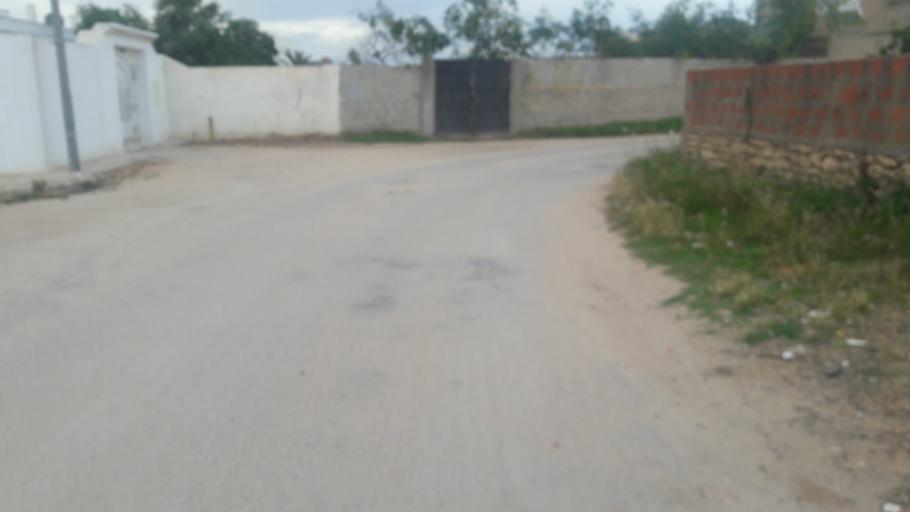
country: TN
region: Safaqis
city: Al Qarmadah
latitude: 34.8104
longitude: 10.7471
